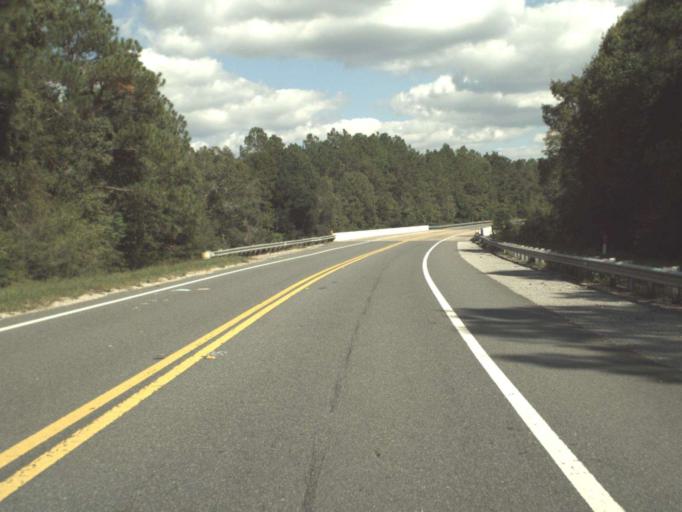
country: US
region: Florida
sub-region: Bay County
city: Laguna Beach
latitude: 30.4476
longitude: -85.8430
